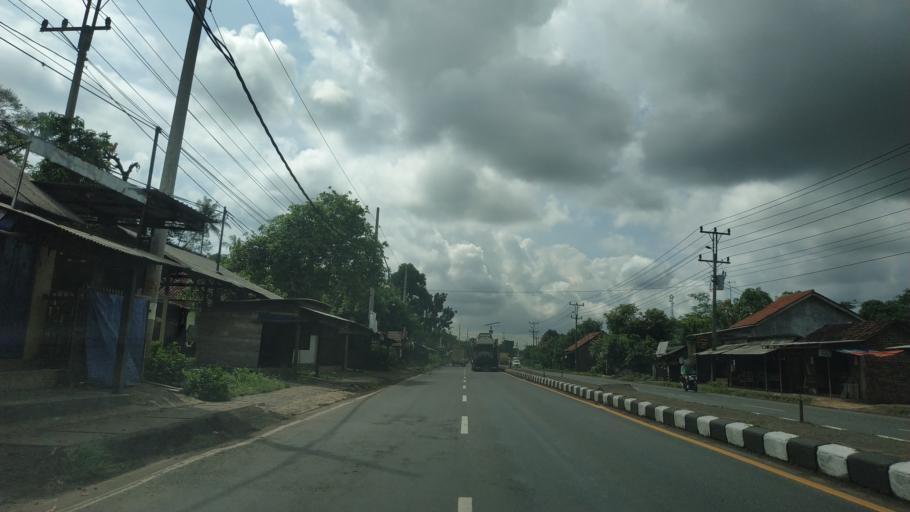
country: ID
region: Central Java
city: Pekalongan
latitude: -6.9476
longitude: 109.7821
